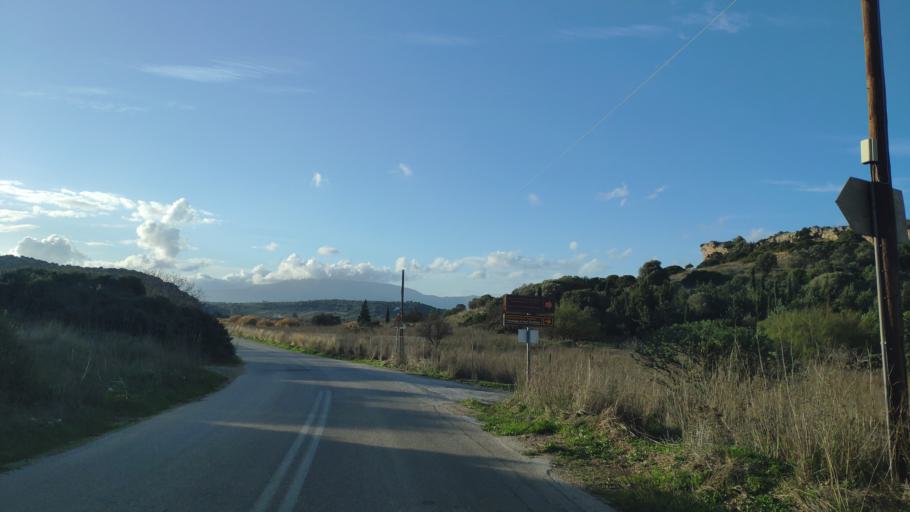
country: GR
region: Attica
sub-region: Nomarchia Anatolikis Attikis
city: Limin Mesoyaias
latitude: 37.9222
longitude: 23.9972
